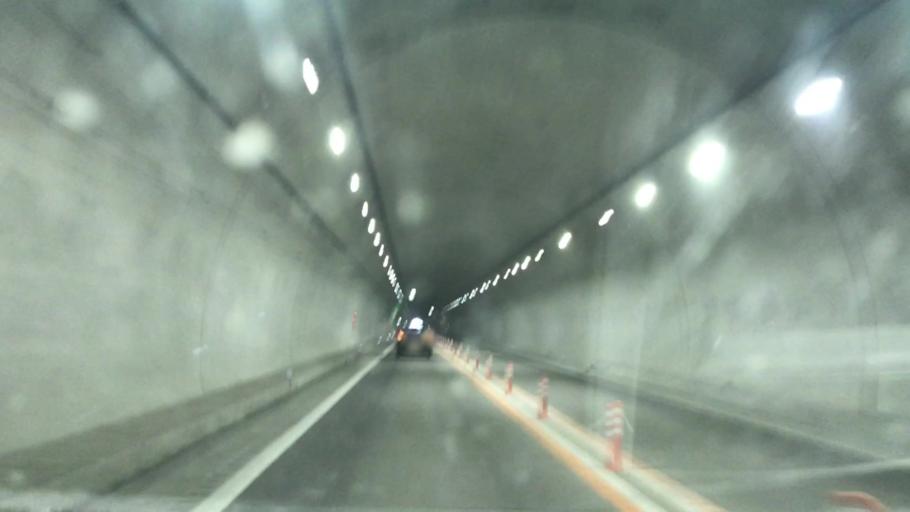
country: JP
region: Hokkaido
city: Yoichi
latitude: 43.1918
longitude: 140.8617
